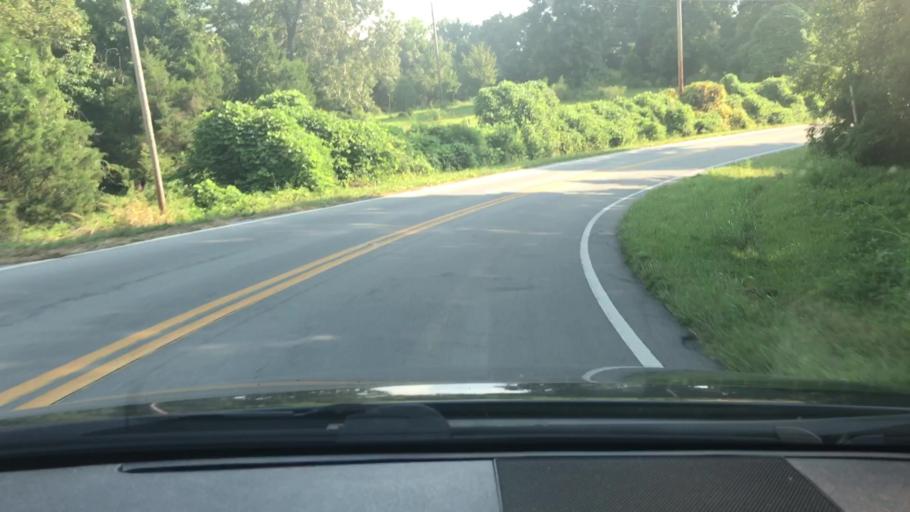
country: US
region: Tennessee
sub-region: Dickson County
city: Charlotte
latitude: 36.2002
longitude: -87.2885
